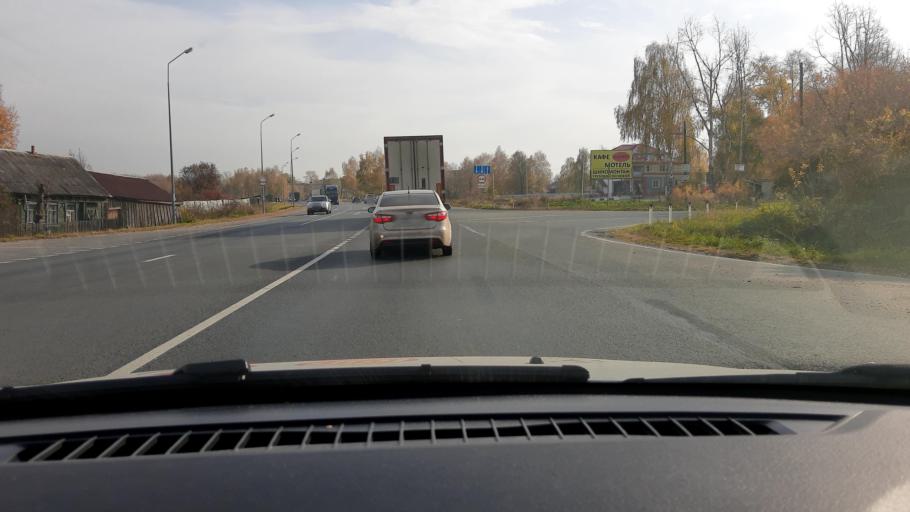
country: RU
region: Nizjnij Novgorod
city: Pamyat' Parizhskoy Kommuny
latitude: 56.0435
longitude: 44.4403
